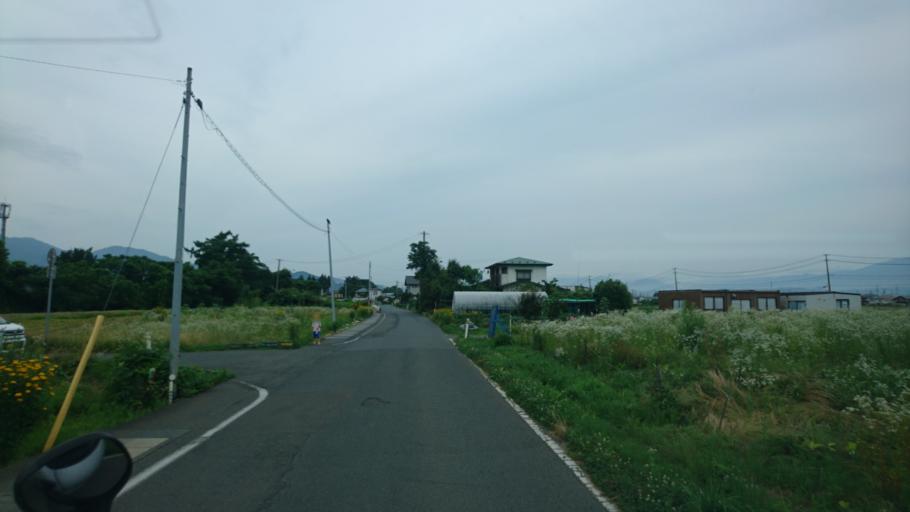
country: JP
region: Iwate
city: Morioka-shi
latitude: 39.6676
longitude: 141.1465
